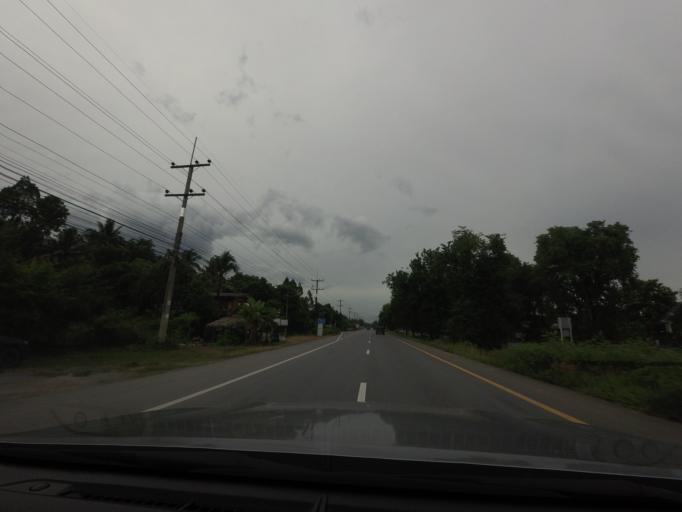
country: TH
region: Nakhon Si Thammarat
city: Chaloem Phra Kiat
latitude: 8.1796
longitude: 100.0409
